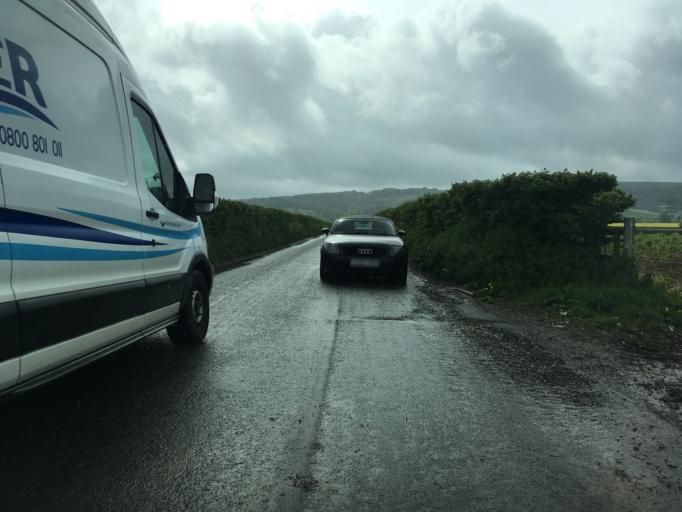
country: GB
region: England
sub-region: North Somerset
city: Burrington
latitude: 51.3430
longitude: -2.7490
